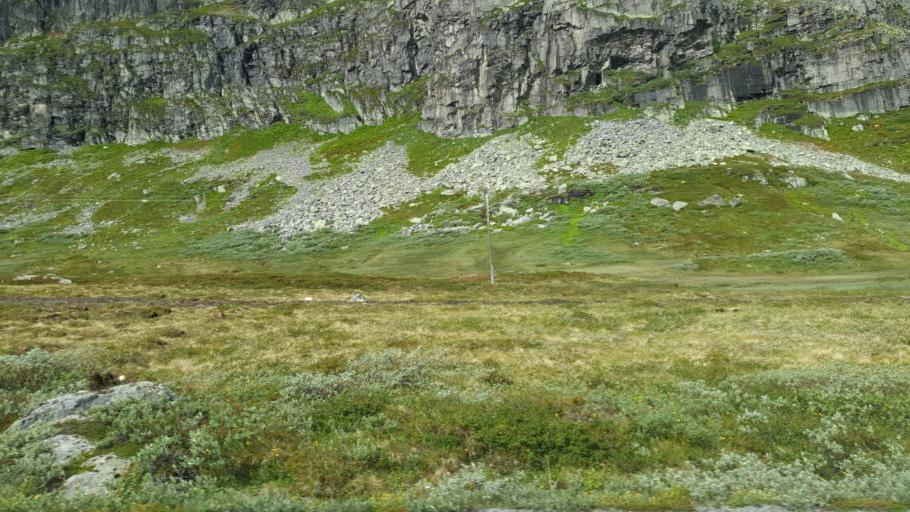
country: NO
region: Oppland
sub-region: Vestre Slidre
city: Slidre
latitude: 61.3044
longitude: 8.8078
